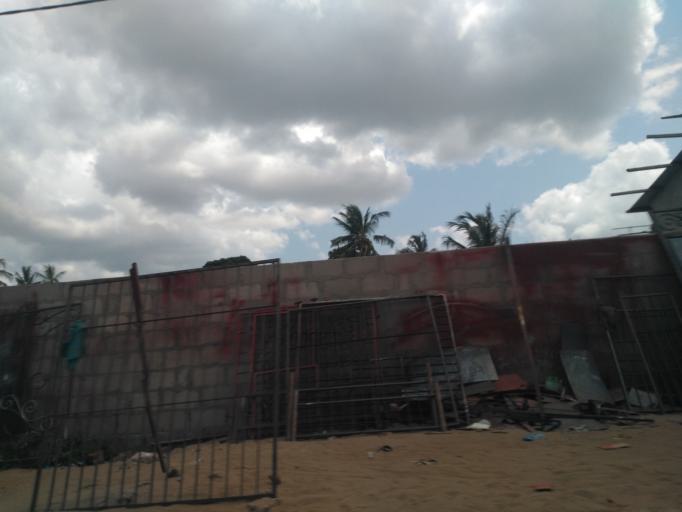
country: TZ
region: Dar es Salaam
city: Dar es Salaam
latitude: -6.8779
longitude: 39.3444
